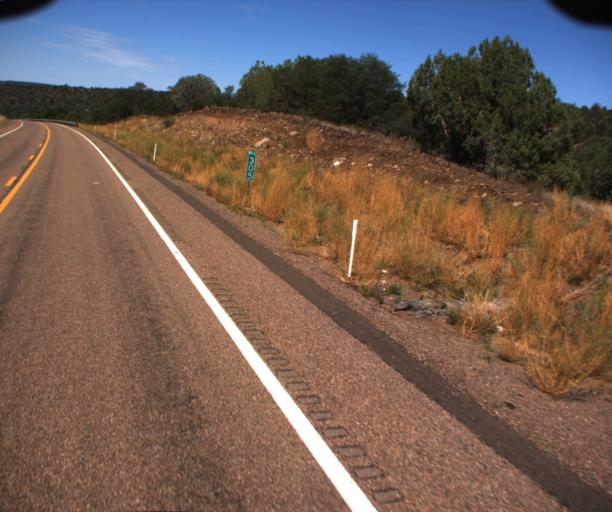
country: US
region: Arizona
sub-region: Navajo County
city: Cibecue
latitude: 33.8921
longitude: -110.3786
